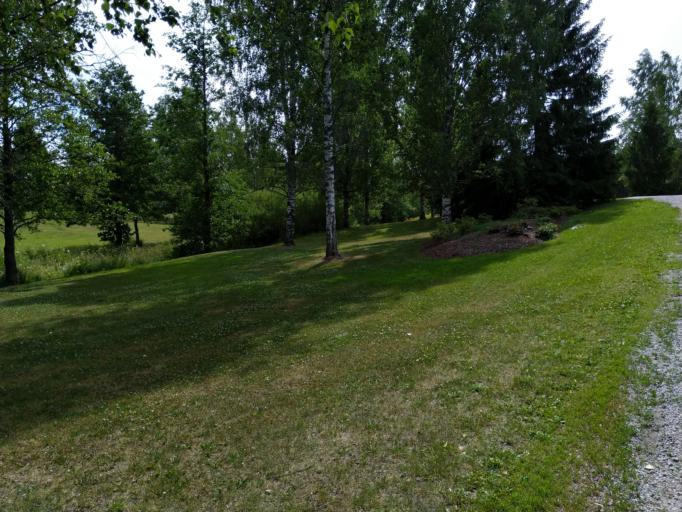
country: FI
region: Varsinais-Suomi
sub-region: Salo
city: Halikko
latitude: 60.3994
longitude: 23.0820
